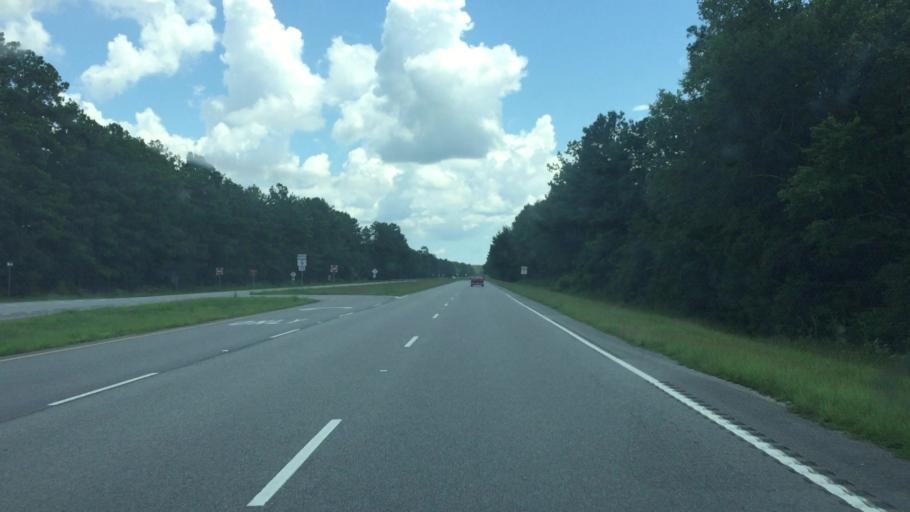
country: US
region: South Carolina
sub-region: Horry County
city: Loris
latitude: 34.0388
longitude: -78.8178
